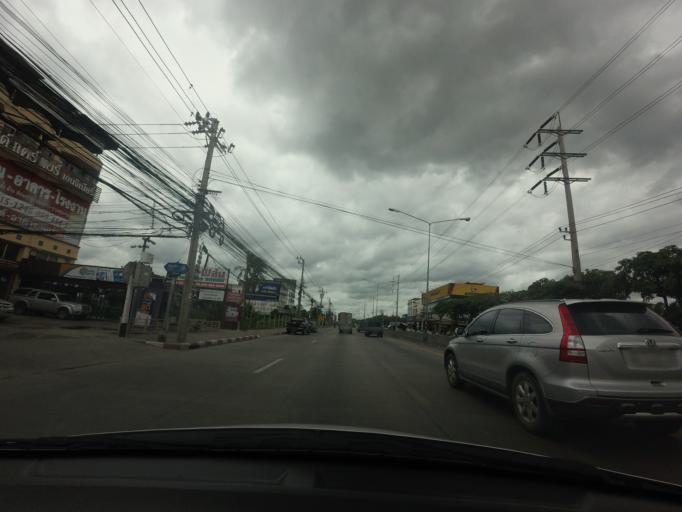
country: TH
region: Bangkok
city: Min Buri
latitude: 13.7778
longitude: 100.7464
